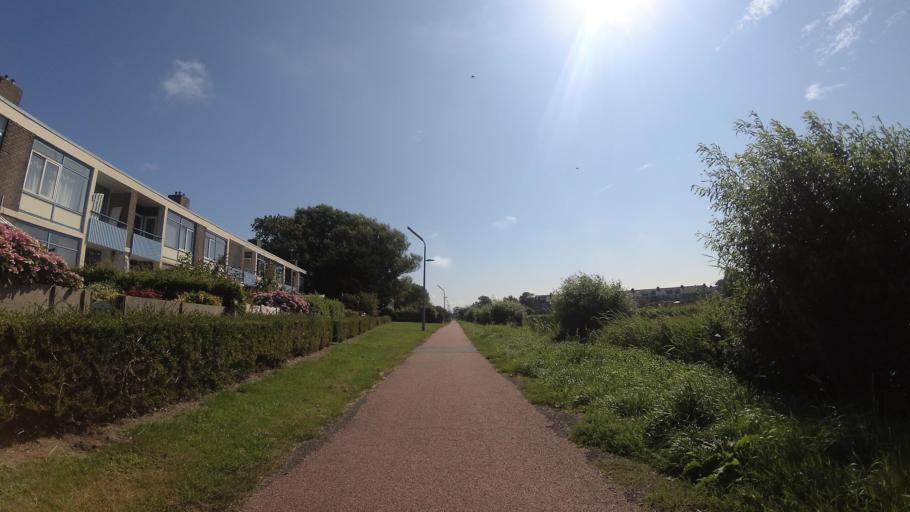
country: NL
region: North Holland
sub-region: Gemeente Den Helder
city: Den Helder
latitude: 52.9352
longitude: 4.7397
